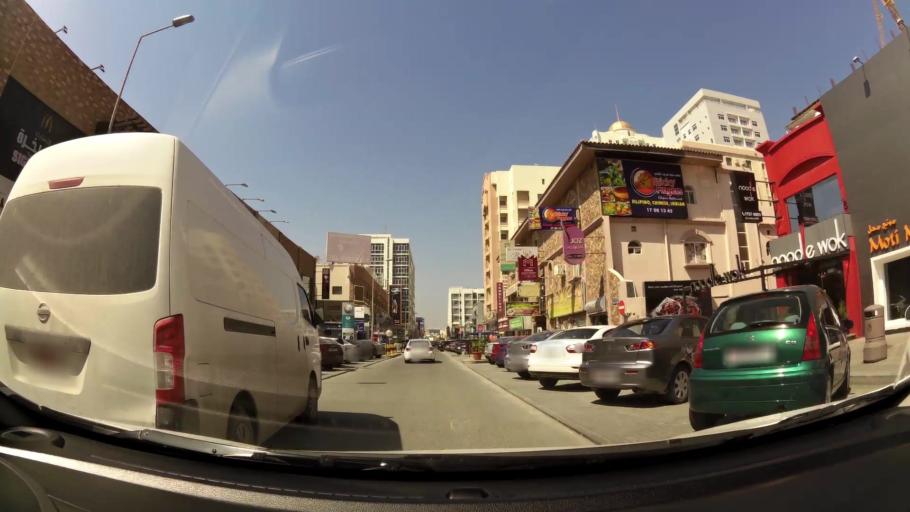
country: BH
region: Manama
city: Manama
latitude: 26.2113
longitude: 50.6085
